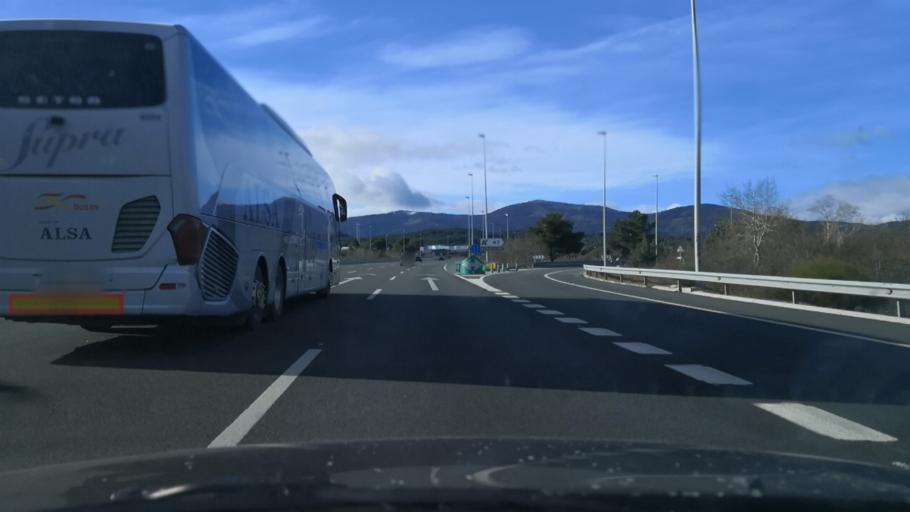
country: ES
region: Madrid
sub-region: Provincia de Madrid
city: Guadarrama
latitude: 40.6566
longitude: -4.0911
